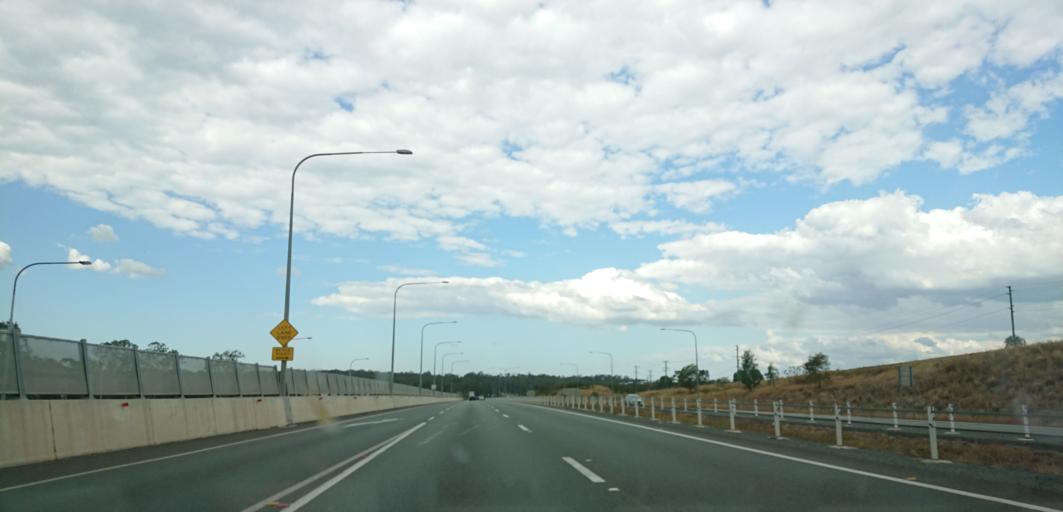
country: AU
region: Queensland
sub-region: Ipswich
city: Brassall
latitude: -27.5769
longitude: 152.7054
